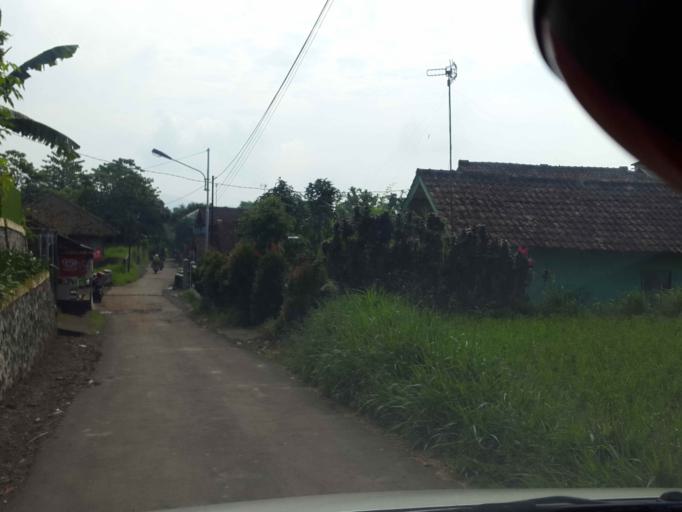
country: ID
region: West Java
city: Sukabumi
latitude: -6.8990
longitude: 106.9638
